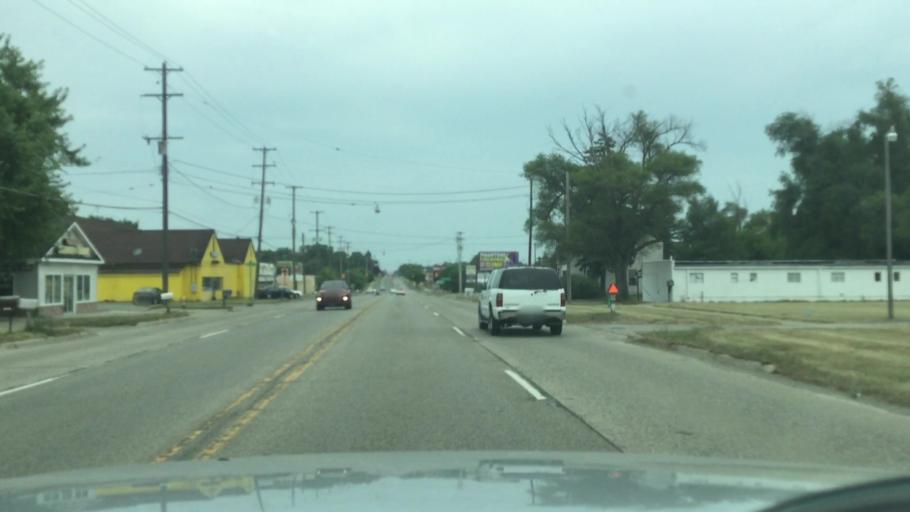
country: US
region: Michigan
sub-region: Genesee County
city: Flint
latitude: 42.9712
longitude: -83.6928
